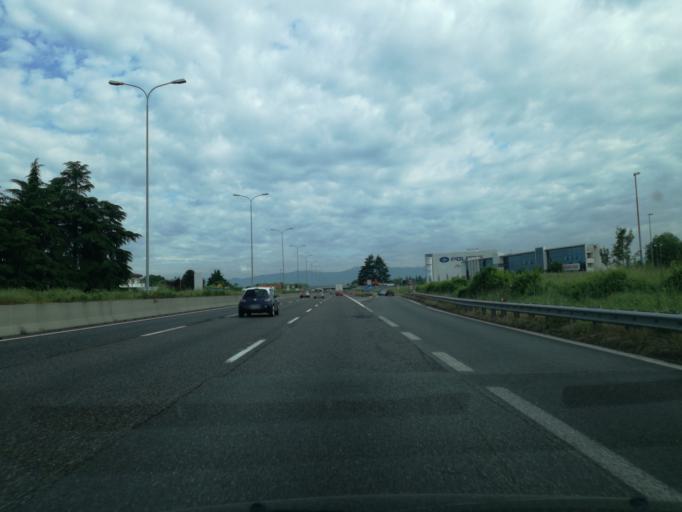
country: IT
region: Lombardy
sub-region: Provincia di Monza e Brianza
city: Carate Brianza
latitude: 45.6586
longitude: 9.2253
